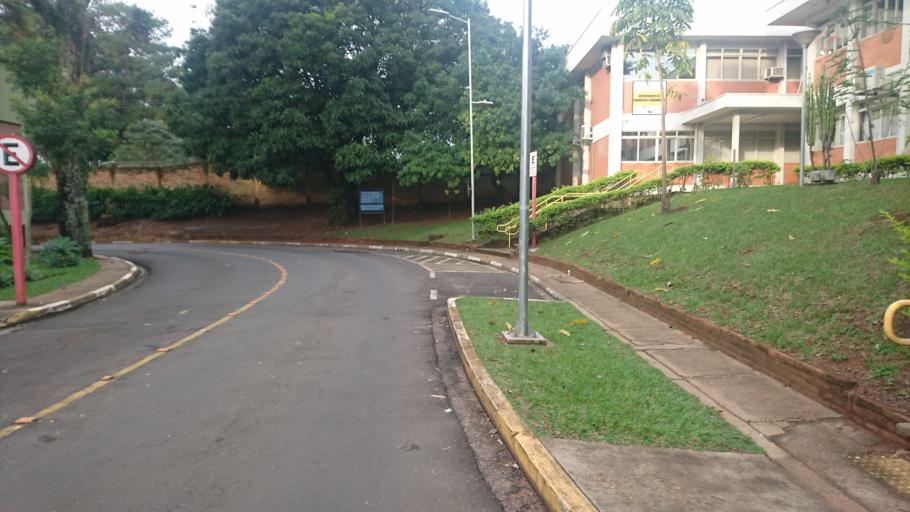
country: BR
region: Sao Paulo
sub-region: Sao Carlos
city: Sao Carlos
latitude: -22.0090
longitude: -47.8963
